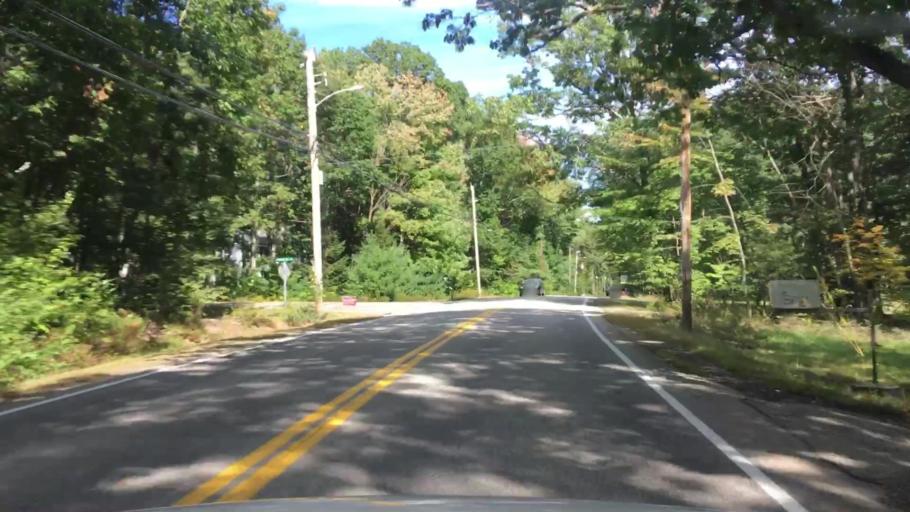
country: US
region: Maine
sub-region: Cumberland County
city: West Scarborough
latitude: 43.6029
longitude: -70.4219
